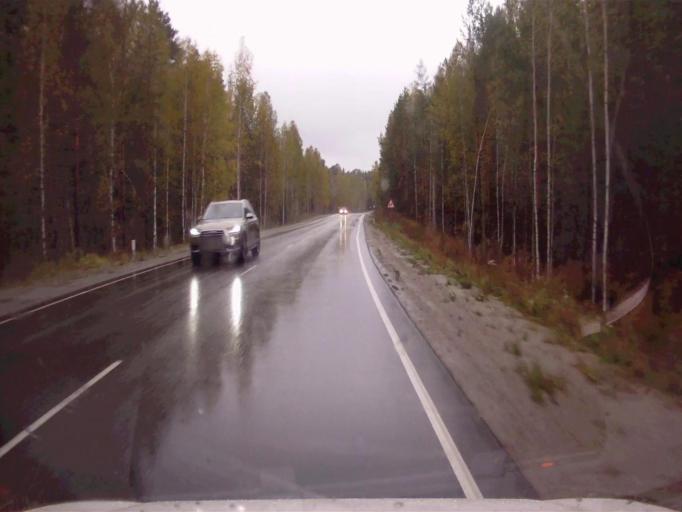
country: RU
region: Chelyabinsk
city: Kyshtym
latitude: 55.6534
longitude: 60.5763
